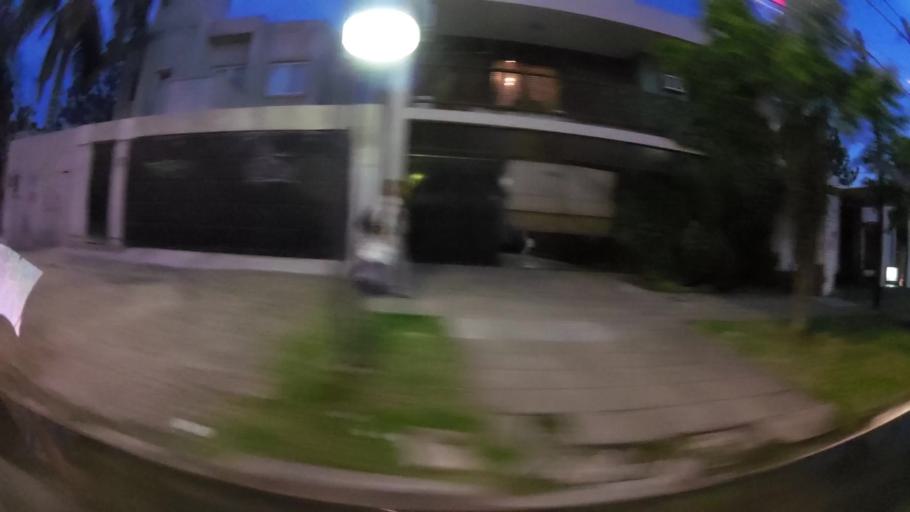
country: AR
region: Buenos Aires
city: Ituzaingo
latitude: -34.6519
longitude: -58.6588
